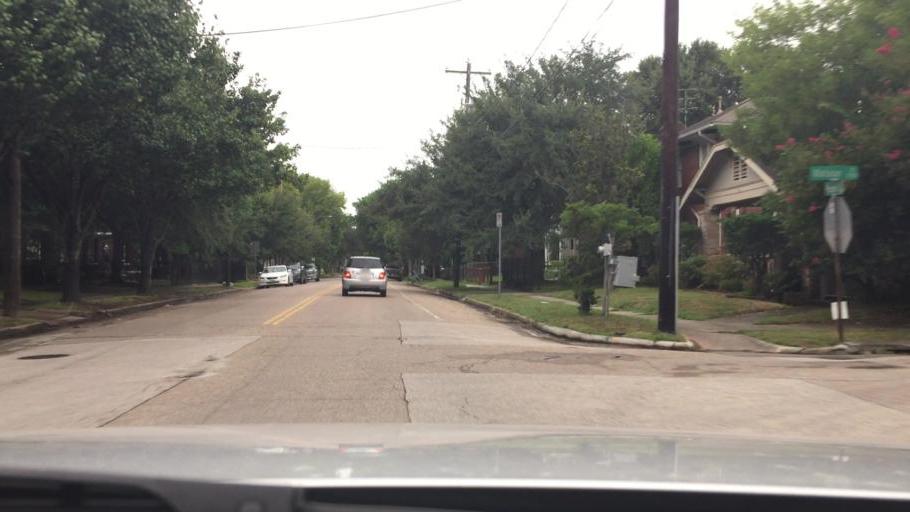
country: US
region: Texas
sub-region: Harris County
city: Houston
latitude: 29.7906
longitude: -95.3809
